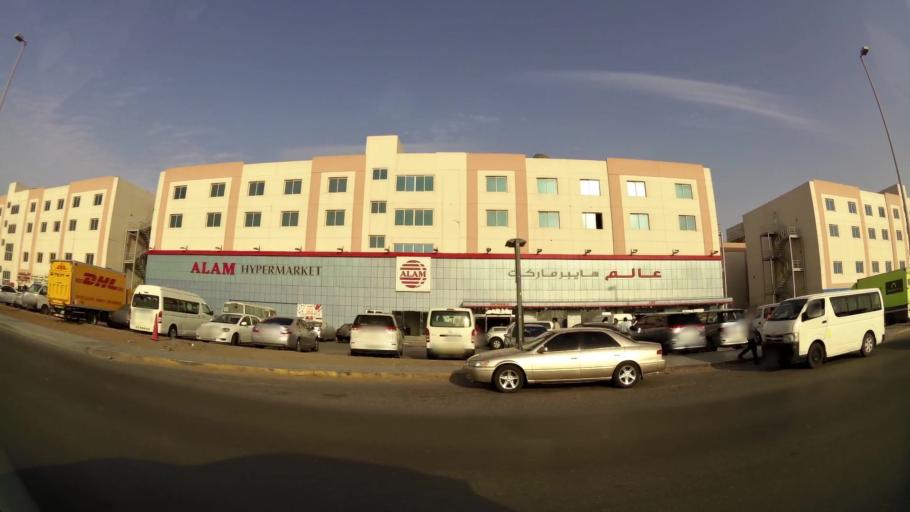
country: AE
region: Abu Dhabi
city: Abu Dhabi
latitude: 24.3623
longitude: 54.5163
